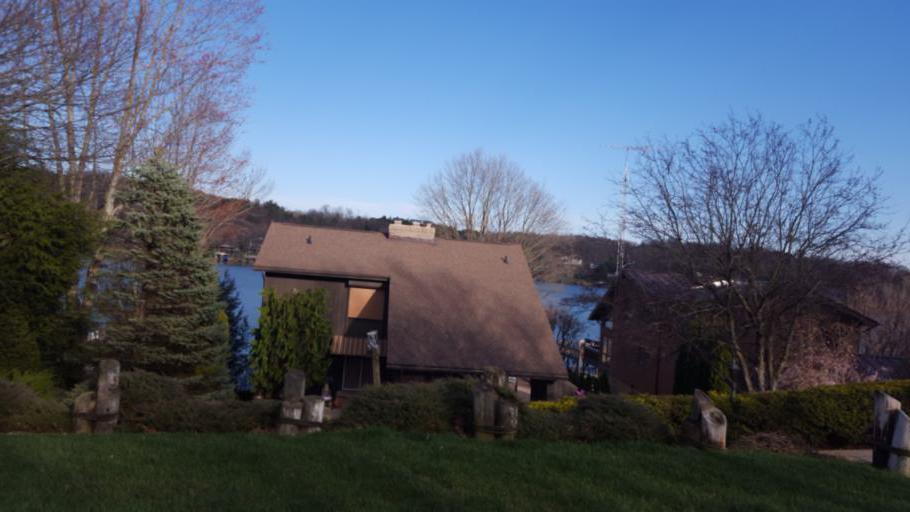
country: US
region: Ohio
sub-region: Knox County
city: Gambier
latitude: 40.4358
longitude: -82.3499
